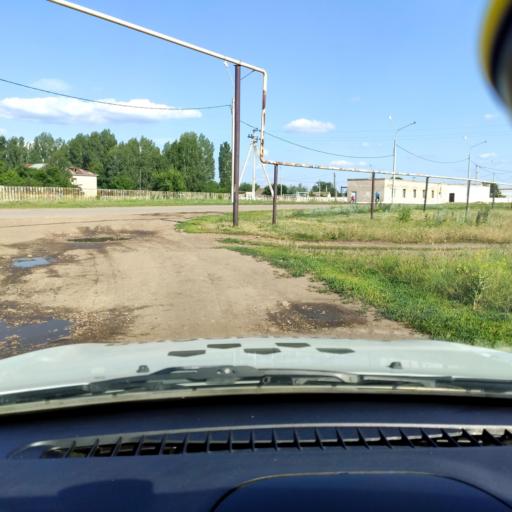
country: RU
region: Samara
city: Tol'yatti
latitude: 53.3530
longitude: 49.2964
